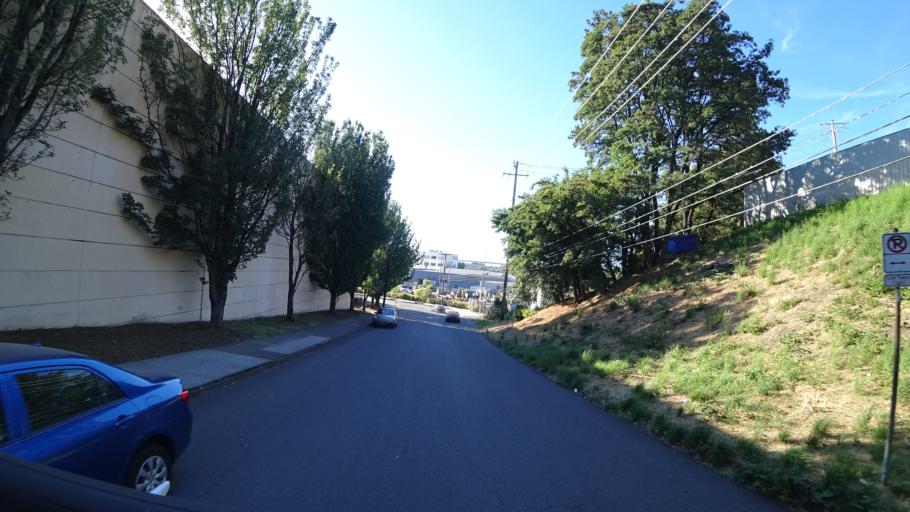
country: US
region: Oregon
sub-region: Multnomah County
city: Portland
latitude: 45.5361
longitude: -122.6703
